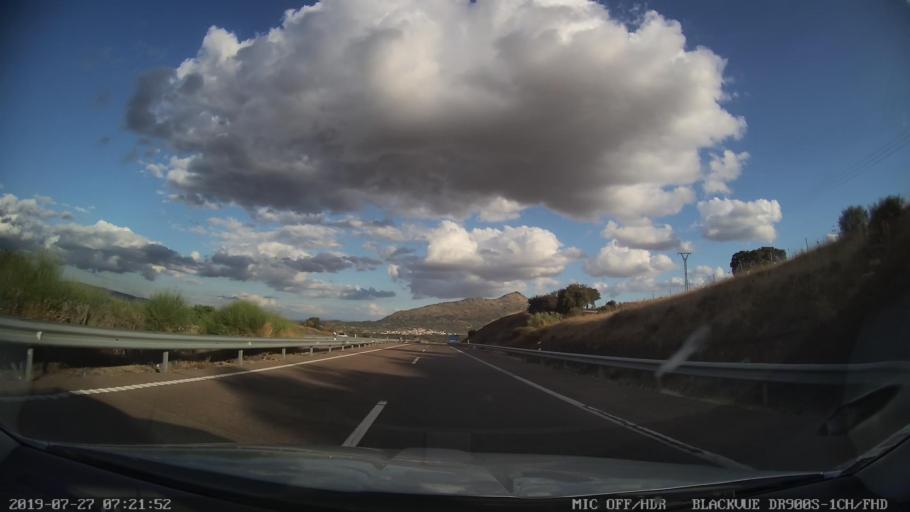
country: ES
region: Extremadura
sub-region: Provincia de Caceres
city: Santa Cruz de la Sierra
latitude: 39.3542
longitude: -5.8617
